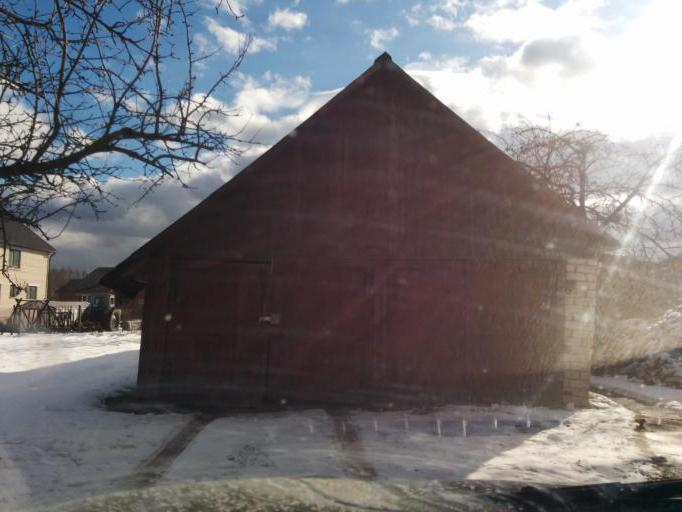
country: LV
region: Balvu Rajons
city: Balvi
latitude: 57.1431
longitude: 27.2630
